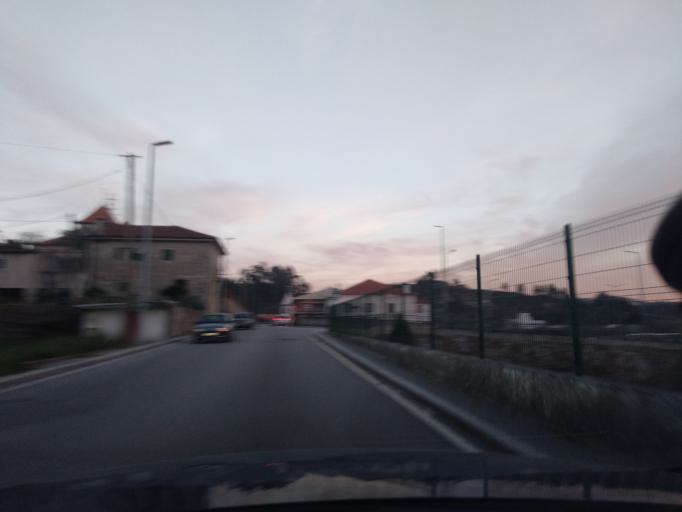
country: PT
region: Porto
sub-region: Paredes
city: Lordelo
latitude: 41.2357
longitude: -8.4116
